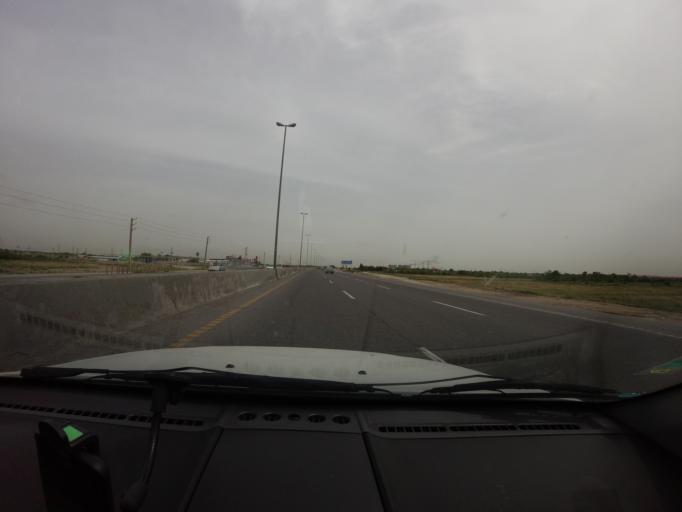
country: IR
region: Tehran
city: Robat Karim
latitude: 35.5197
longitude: 51.0791
